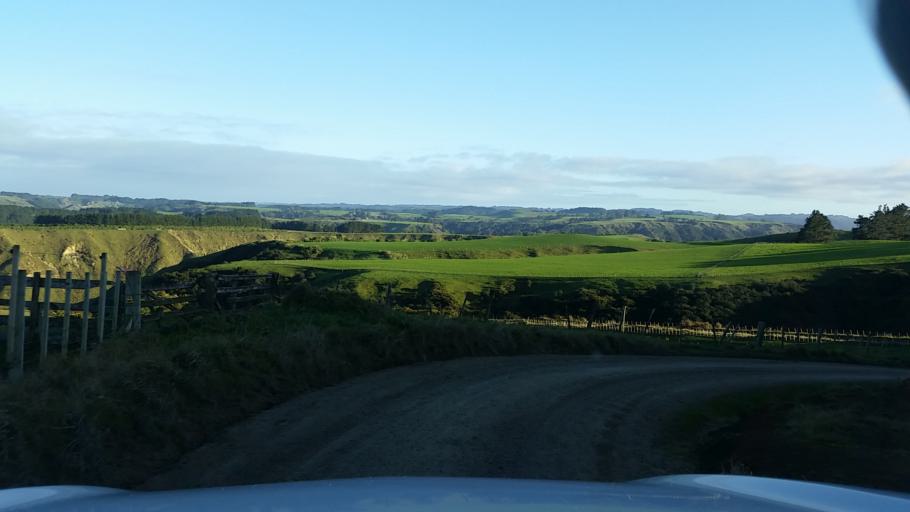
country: NZ
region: Taranaki
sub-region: South Taranaki District
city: Patea
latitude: -39.7559
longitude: 174.7474
